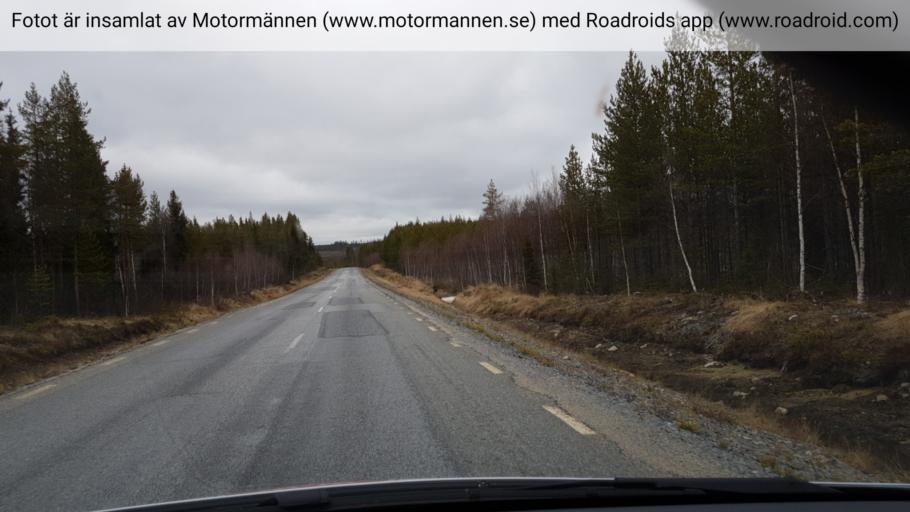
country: SE
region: Vaesternorrland
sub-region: OErnskoeldsviks Kommun
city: Bredbyn
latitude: 63.9611
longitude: 18.4959
